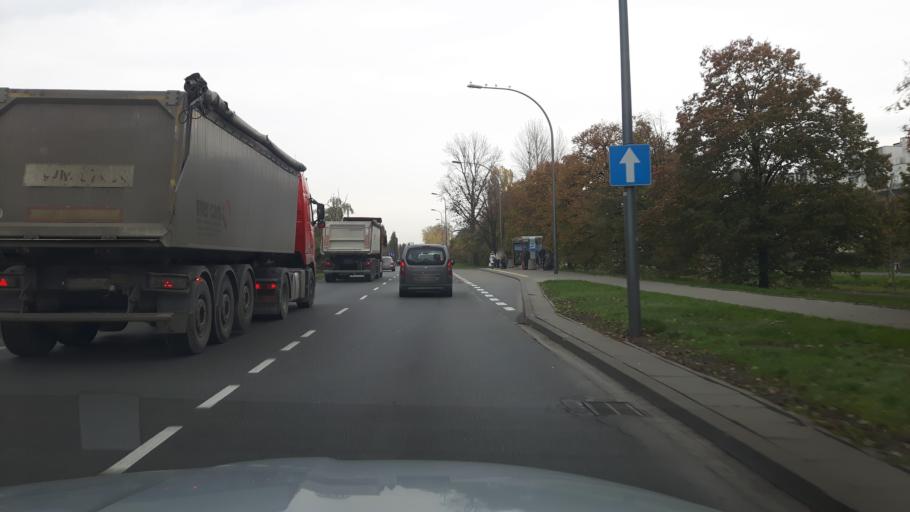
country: PL
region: Masovian Voivodeship
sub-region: Warszawa
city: Wilanow
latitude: 52.1679
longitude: 21.0757
